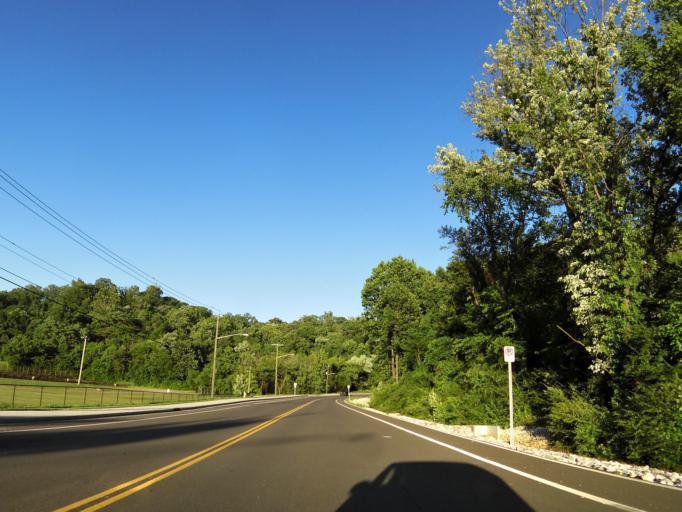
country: US
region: Tennessee
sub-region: Knox County
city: Knoxville
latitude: 36.0022
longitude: -83.8816
